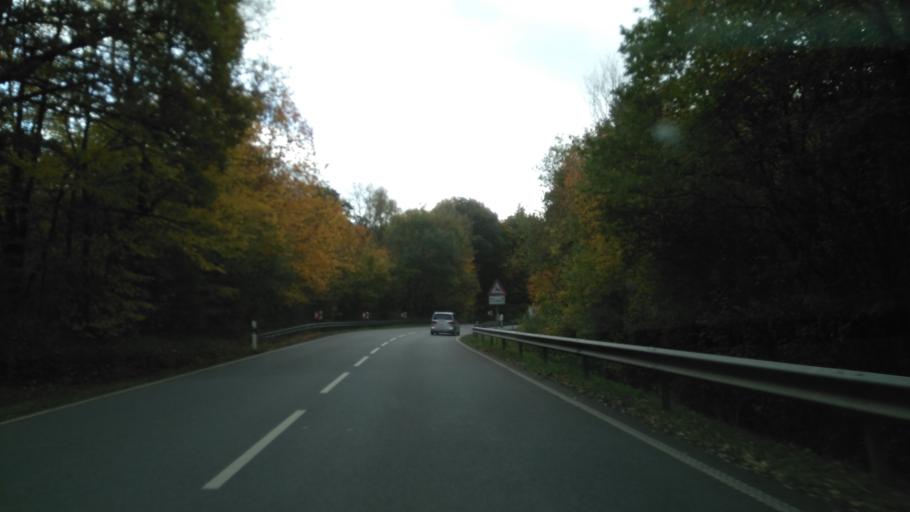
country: DE
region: Rheinland-Pfalz
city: Trier
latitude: 49.7118
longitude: 6.6302
